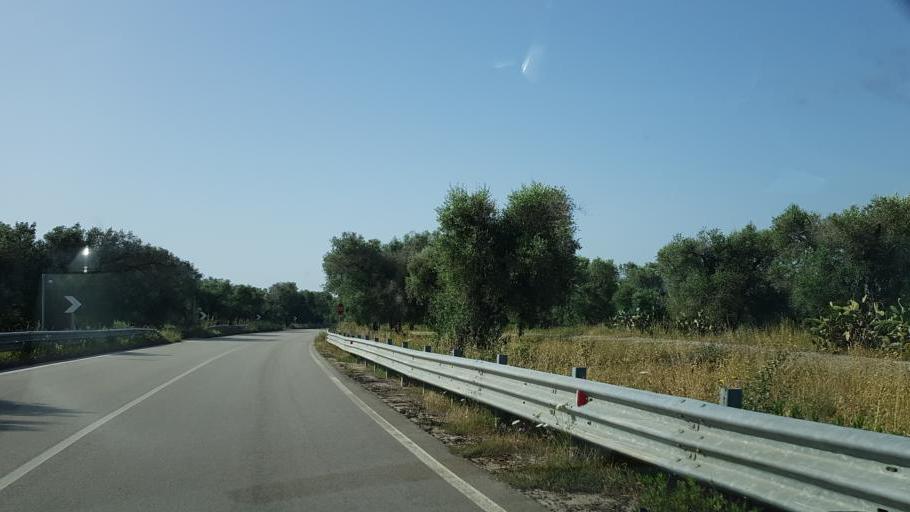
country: IT
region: Apulia
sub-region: Provincia di Brindisi
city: Mesagne
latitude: 40.4928
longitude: 17.8327
